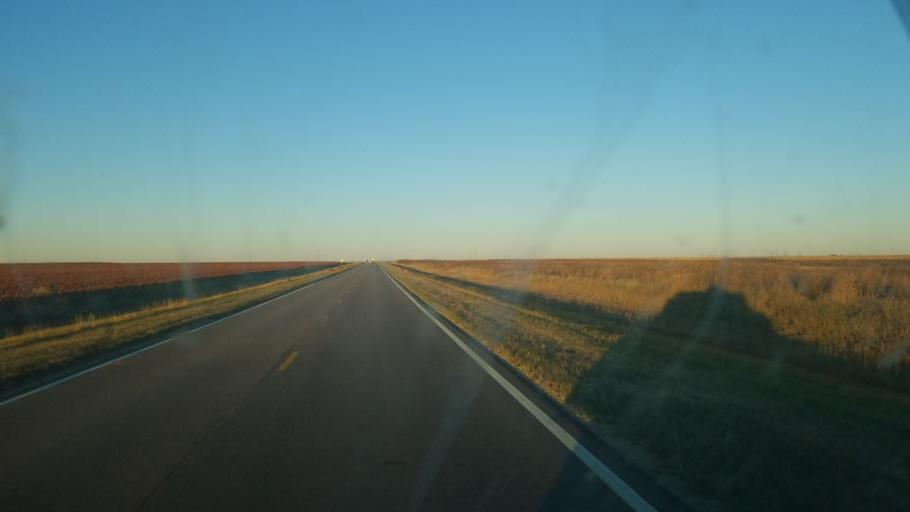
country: US
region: Kansas
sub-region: Wallace County
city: Sharon Springs
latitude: 38.8675
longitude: -101.9757
